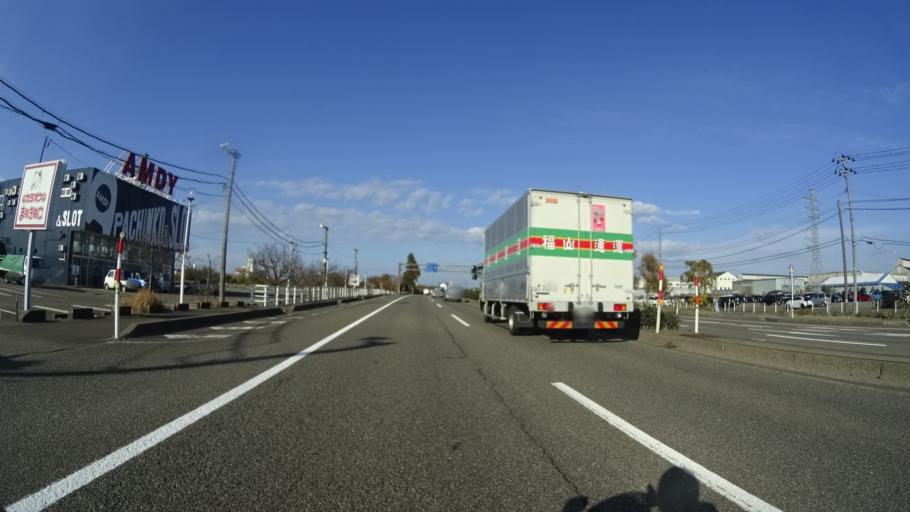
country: JP
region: Niigata
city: Joetsu
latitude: 37.1733
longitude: 138.2660
